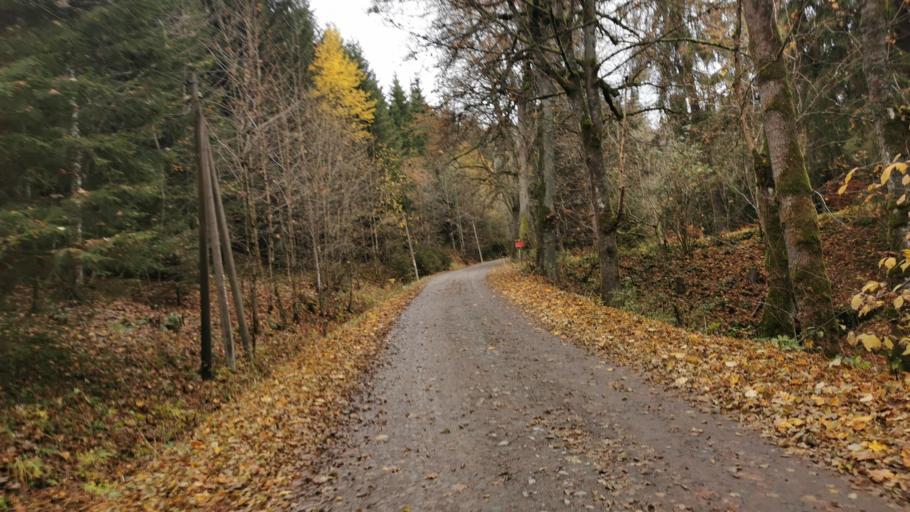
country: DE
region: Thuringia
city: Wurzbach
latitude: 50.4473
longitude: 11.5483
